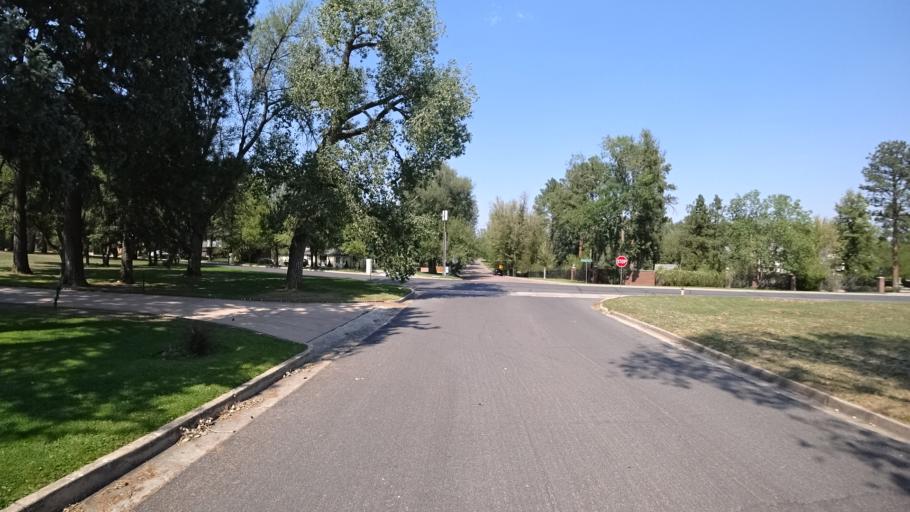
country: US
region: Colorado
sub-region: El Paso County
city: Colorado Springs
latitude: 38.7882
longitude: -104.8441
